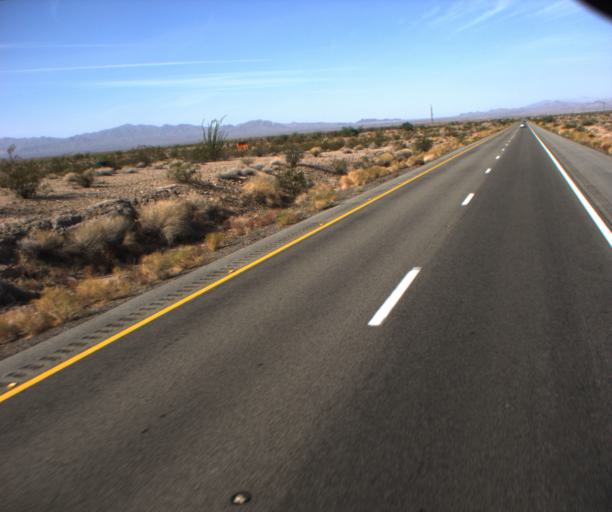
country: US
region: Arizona
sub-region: Mohave County
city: Desert Hills
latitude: 34.7859
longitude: -114.1736
